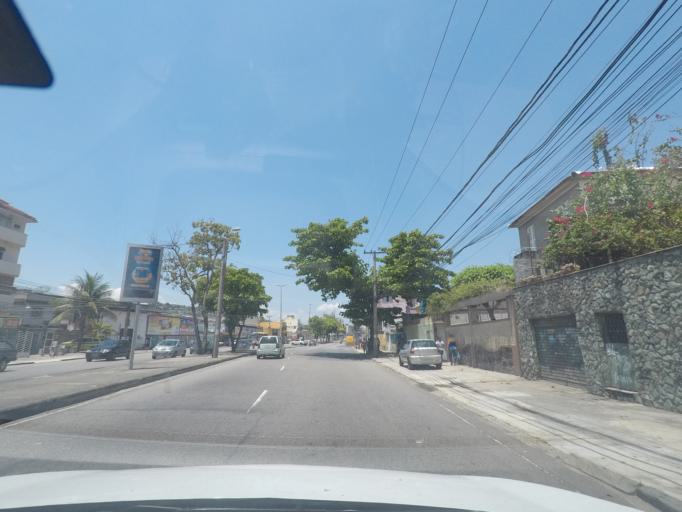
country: BR
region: Rio de Janeiro
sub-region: Rio De Janeiro
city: Rio de Janeiro
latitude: -22.8835
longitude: -43.2966
